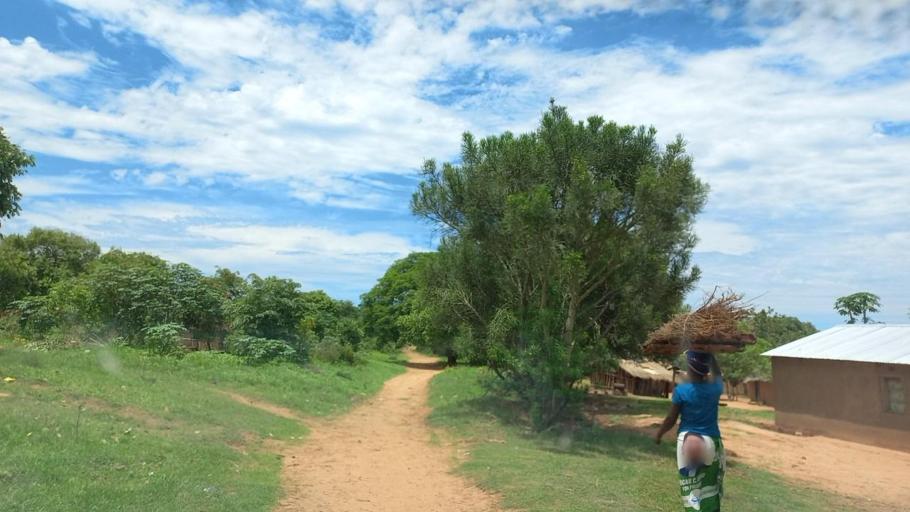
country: ZM
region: North-Western
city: Kabompo
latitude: -13.6103
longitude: 24.2451
